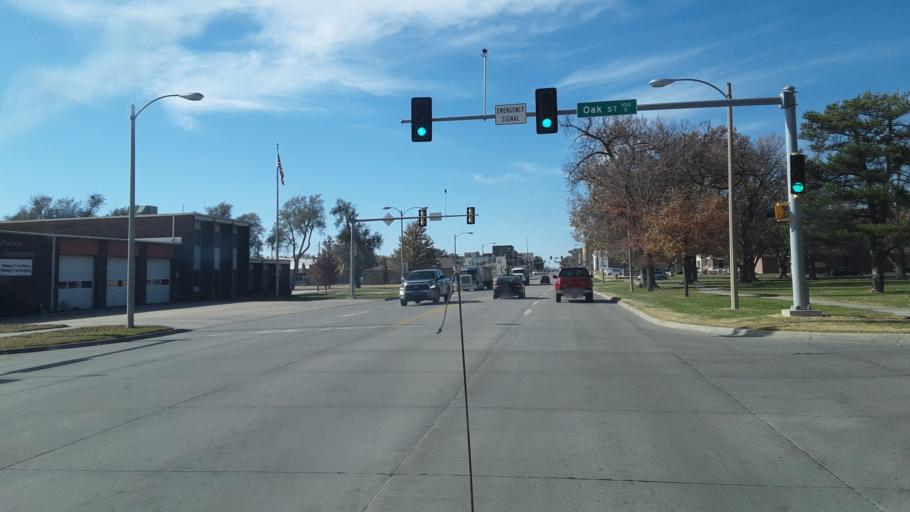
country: US
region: Kansas
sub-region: McPherson County
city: McPherson
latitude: 38.3694
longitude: -97.6627
